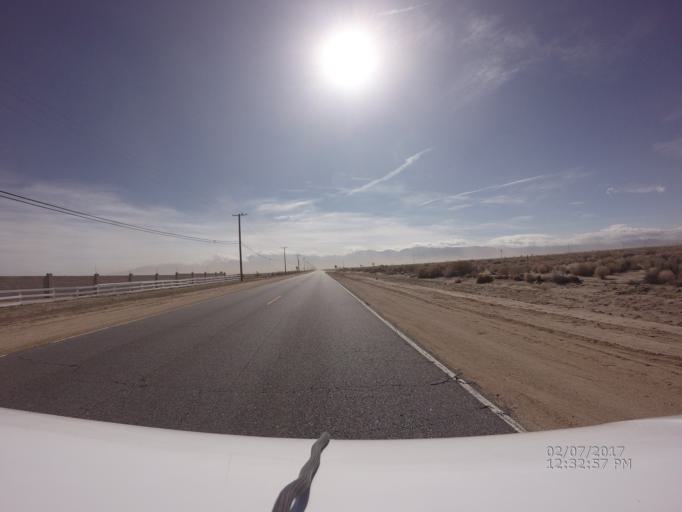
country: US
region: California
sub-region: Los Angeles County
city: Lake Los Angeles
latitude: 34.5898
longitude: -117.8268
